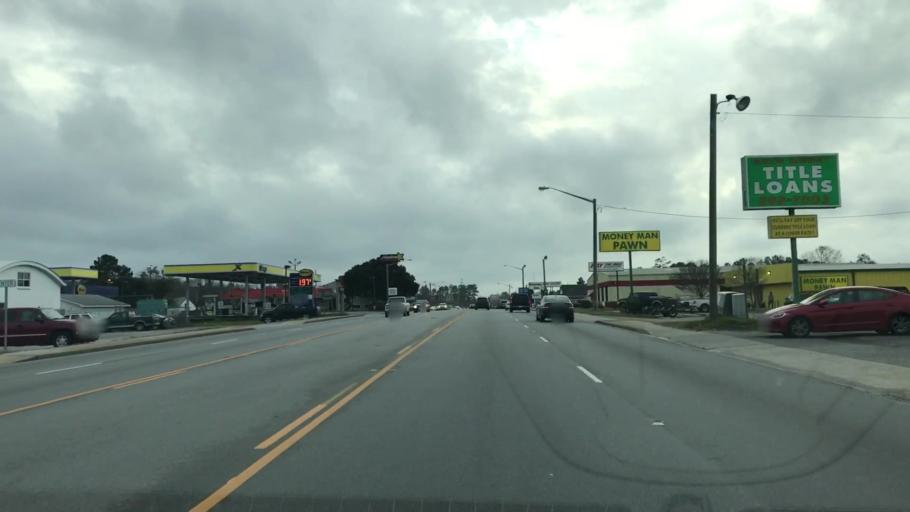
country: US
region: South Carolina
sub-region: Berkeley County
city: Moncks Corner
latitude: 33.2054
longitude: -79.9864
